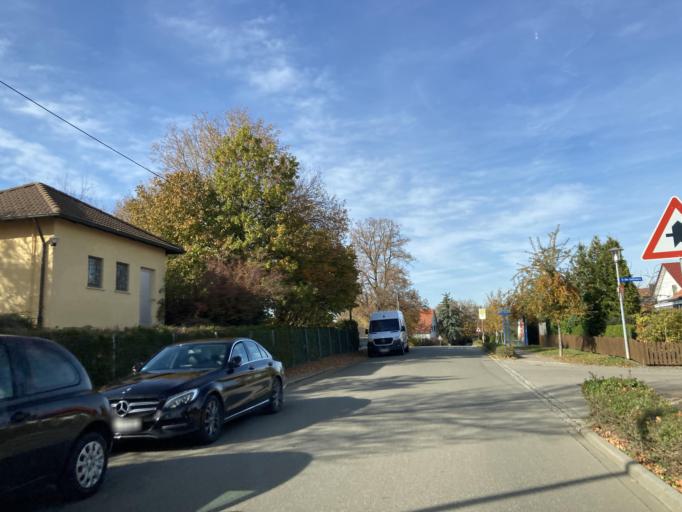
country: DE
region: Baden-Wuerttemberg
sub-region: Tuebingen Region
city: Bodelshausen
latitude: 48.3799
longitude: 8.9731
